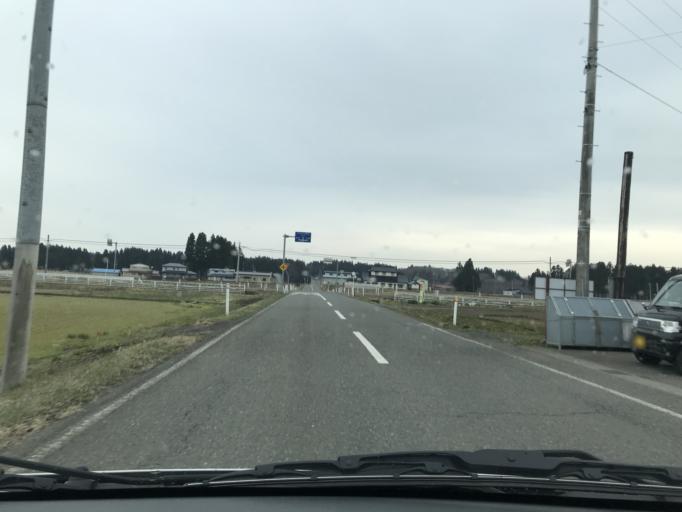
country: JP
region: Iwate
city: Mizusawa
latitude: 39.0997
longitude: 141.0695
